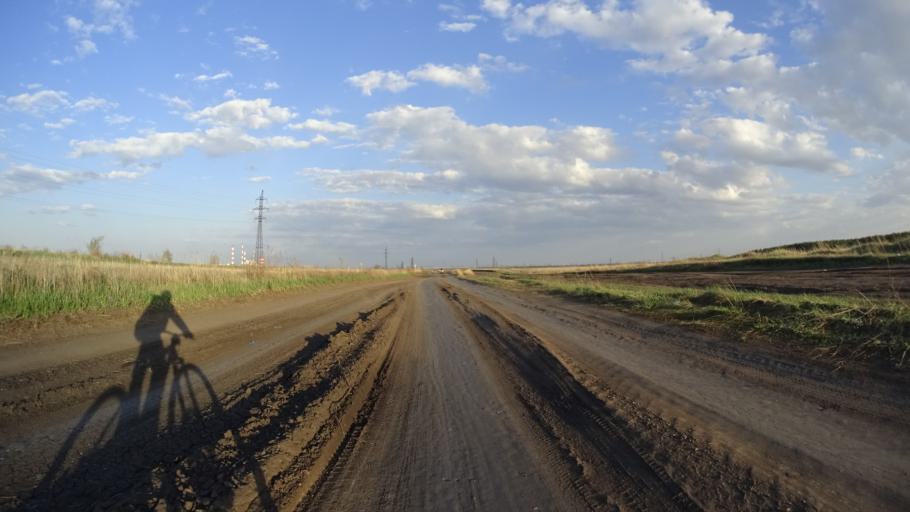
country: RU
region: Chelyabinsk
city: Troitsk
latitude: 54.0512
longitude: 61.5929
